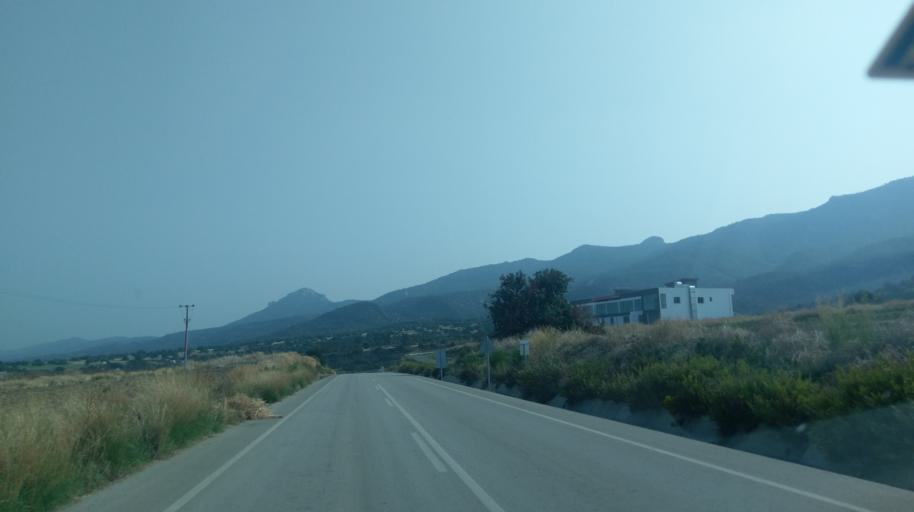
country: CY
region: Ammochostos
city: Trikomo
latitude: 35.4267
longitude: 33.9069
